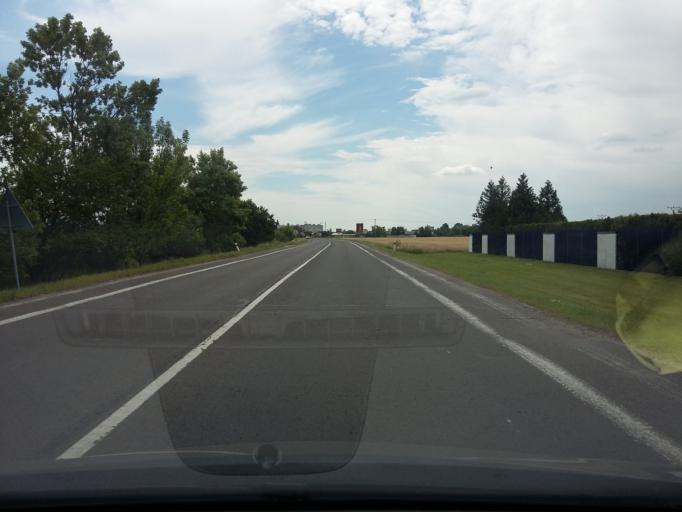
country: SK
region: Bratislavsky
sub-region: Okres Malacky
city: Malacky
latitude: 48.4523
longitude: 17.0107
